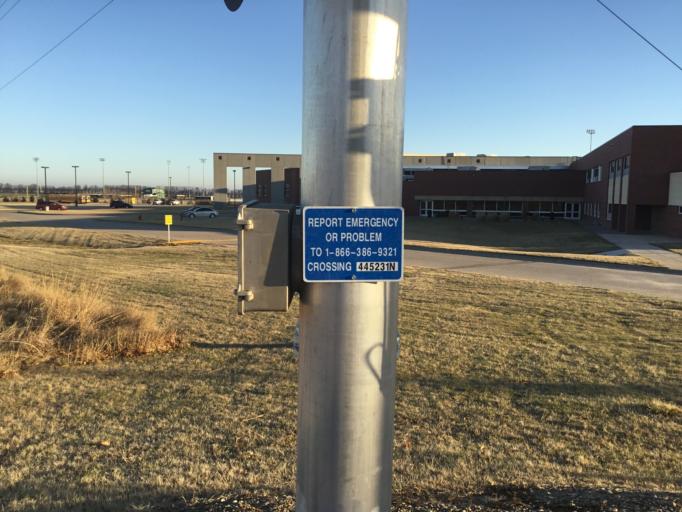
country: US
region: Kansas
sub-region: Sedgwick County
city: Saint Marys
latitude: 37.7933
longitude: -97.6356
